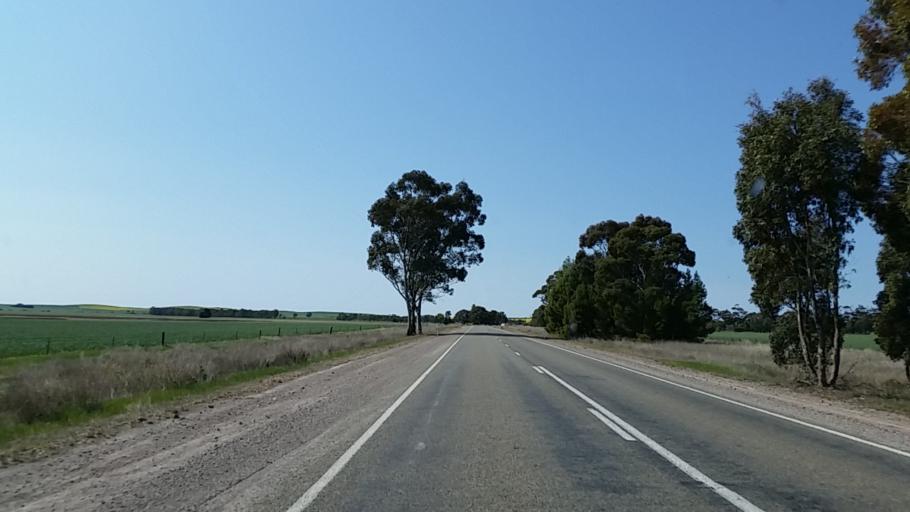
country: AU
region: South Australia
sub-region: Northern Areas
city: Jamestown
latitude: -33.1879
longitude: 138.5055
